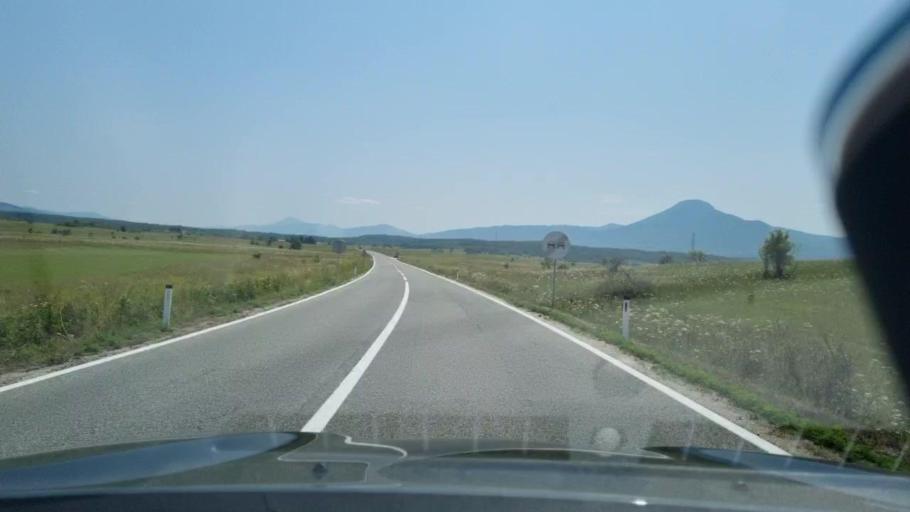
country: BA
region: Federation of Bosnia and Herzegovina
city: Orasac
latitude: 44.6250
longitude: 16.2164
